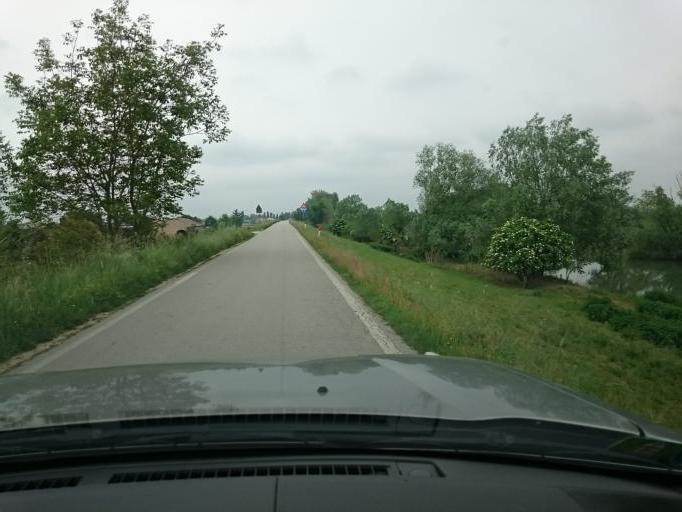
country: IT
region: Veneto
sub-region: Provincia di Padova
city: Campagnola
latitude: 45.2586
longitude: 11.9839
